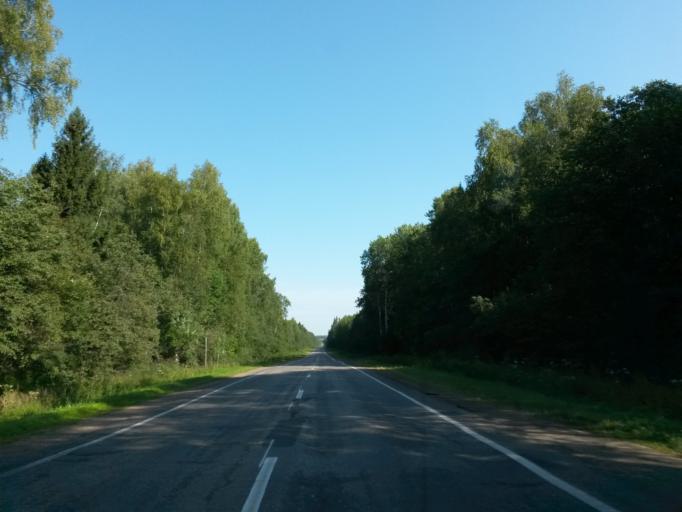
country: RU
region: Jaroslavl
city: Gavrilov-Yam
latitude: 57.4192
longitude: 39.9198
